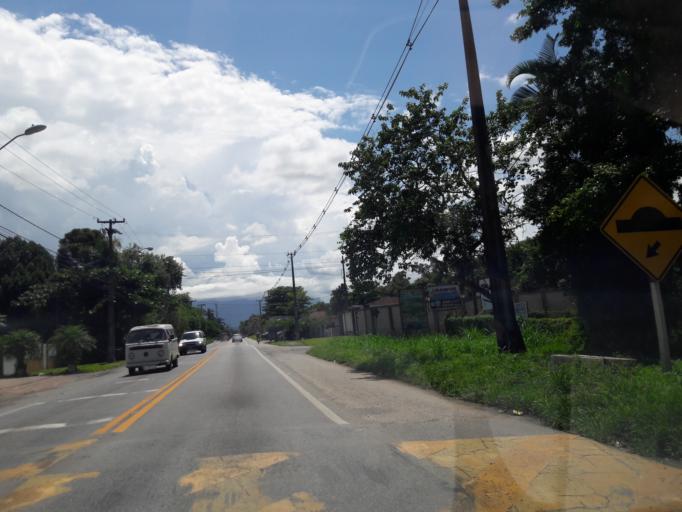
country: BR
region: Parana
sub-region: Antonina
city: Antonina
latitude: -25.4888
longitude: -48.8249
